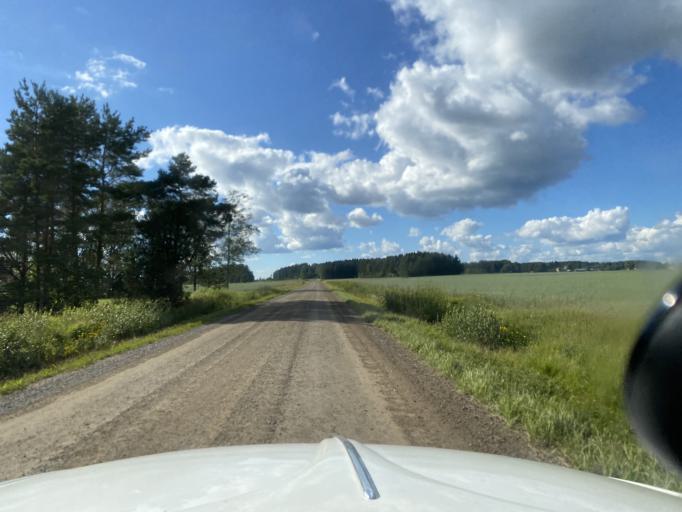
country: FI
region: Pirkanmaa
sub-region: Lounais-Pirkanmaa
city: Punkalaidun
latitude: 61.1345
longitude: 23.2284
